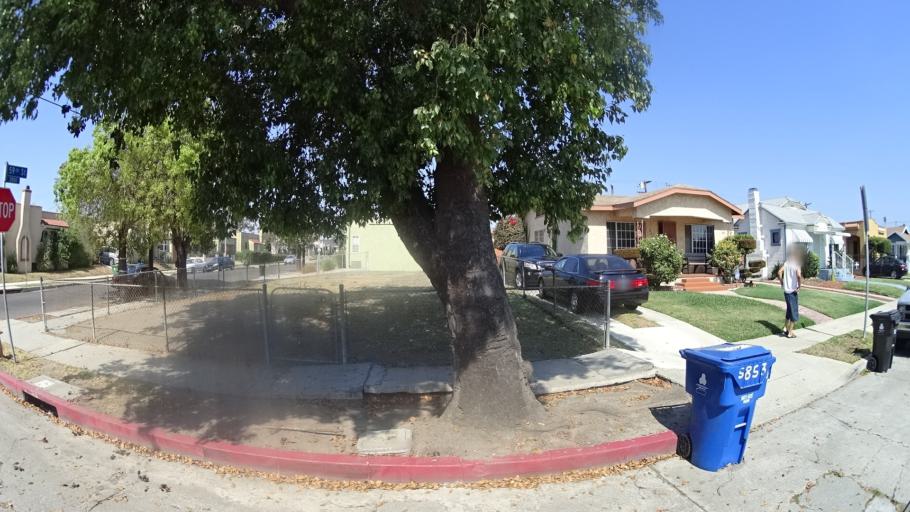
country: US
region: California
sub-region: Los Angeles County
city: View Park-Windsor Hills
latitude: 33.9874
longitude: -118.3235
